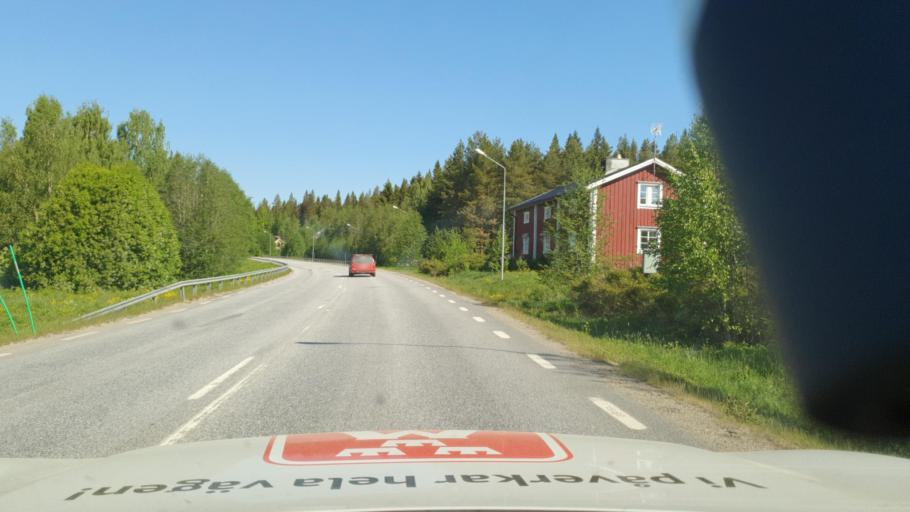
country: SE
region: Vaesterbotten
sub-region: Vannas Kommun
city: Vaennaes
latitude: 63.9630
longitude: 19.7516
